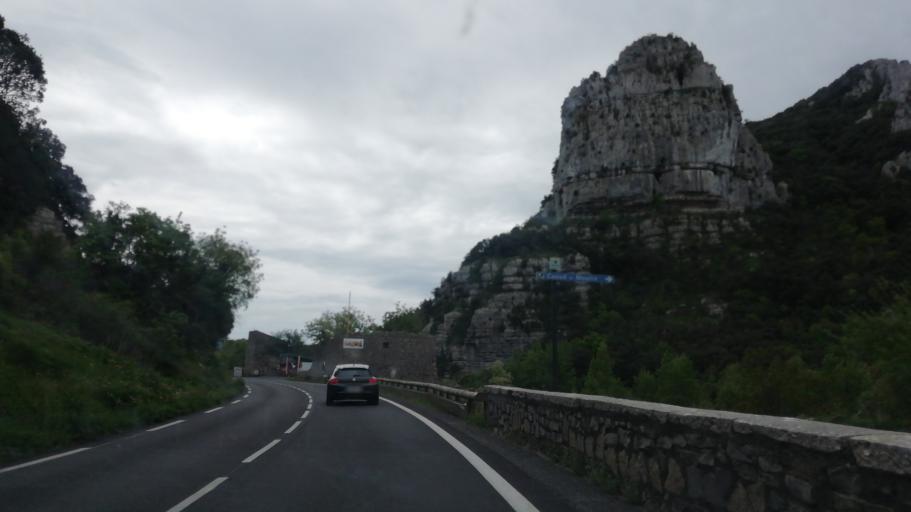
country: FR
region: Languedoc-Roussillon
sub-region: Departement de l'Herault
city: Saint-Bauzille-de-Putois
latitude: 43.9109
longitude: 3.7364
